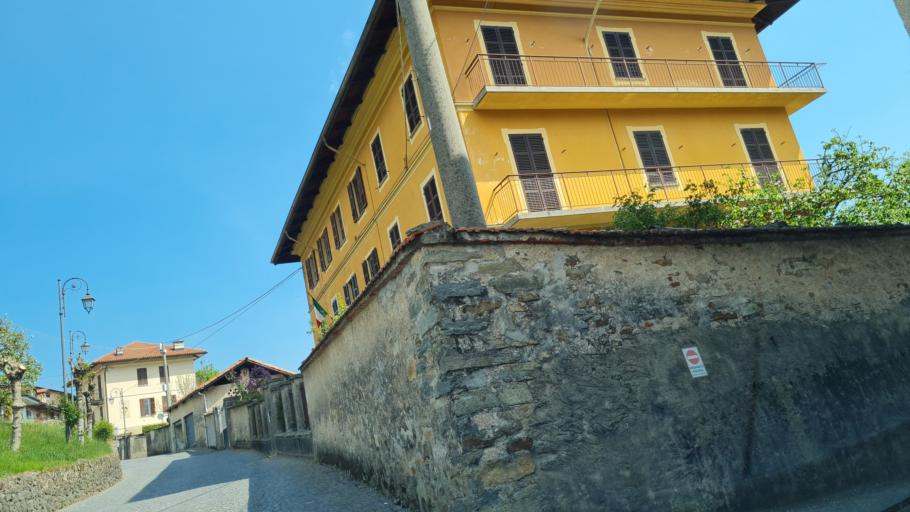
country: IT
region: Piedmont
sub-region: Provincia di Biella
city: Sordevolo
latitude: 45.5740
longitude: 7.9722
